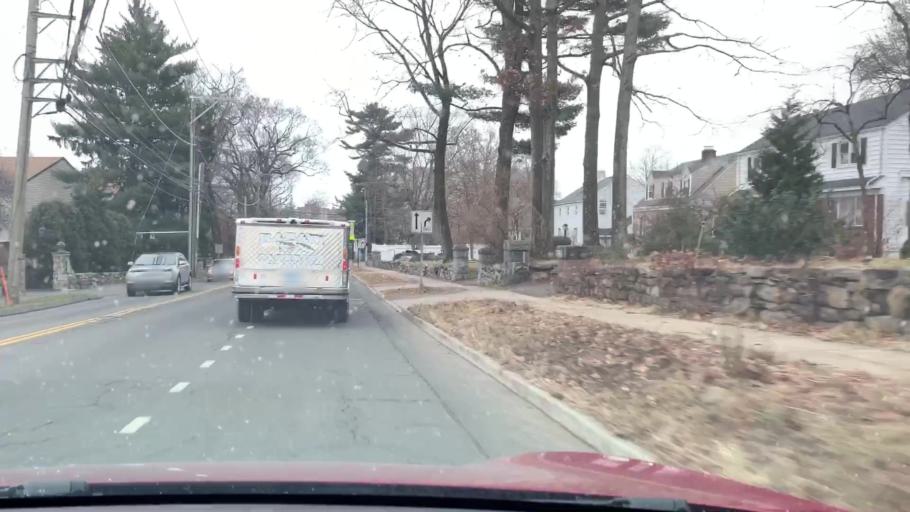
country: US
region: Connecticut
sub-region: Fairfield County
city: Stamford
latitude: 41.0689
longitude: -73.5340
